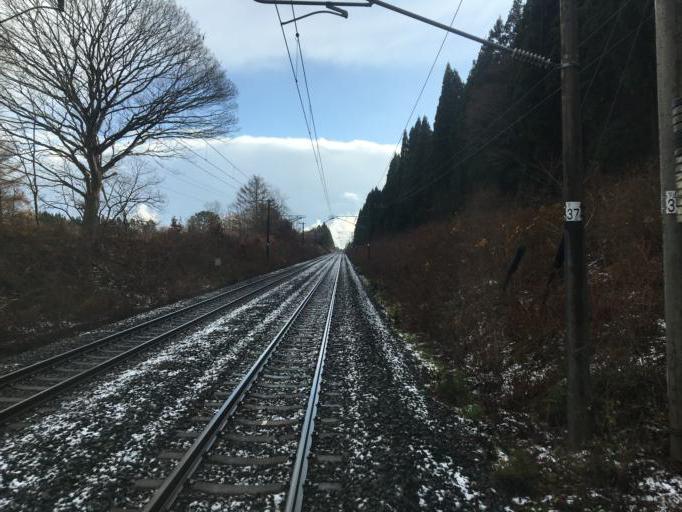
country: JP
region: Aomori
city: Aomori Shi
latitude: 40.9115
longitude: 141.0467
